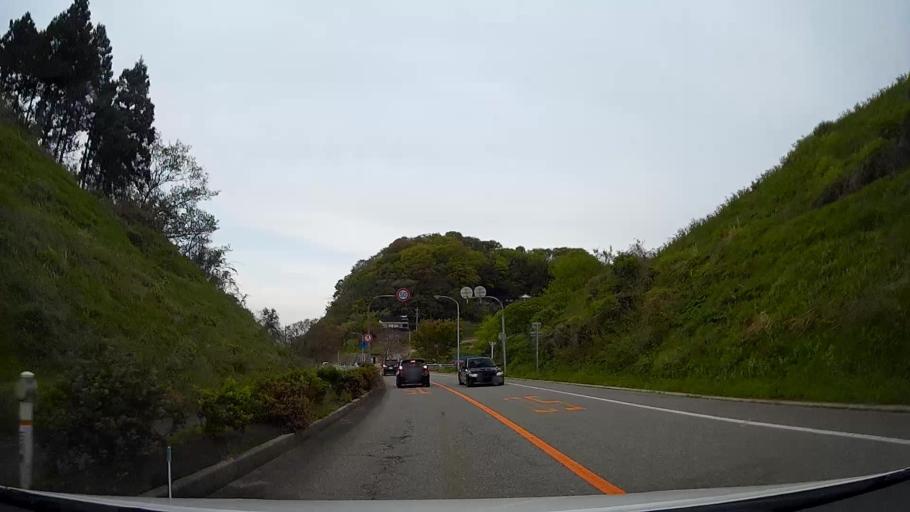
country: JP
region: Ishikawa
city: Nanao
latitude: 37.4072
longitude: 136.9601
